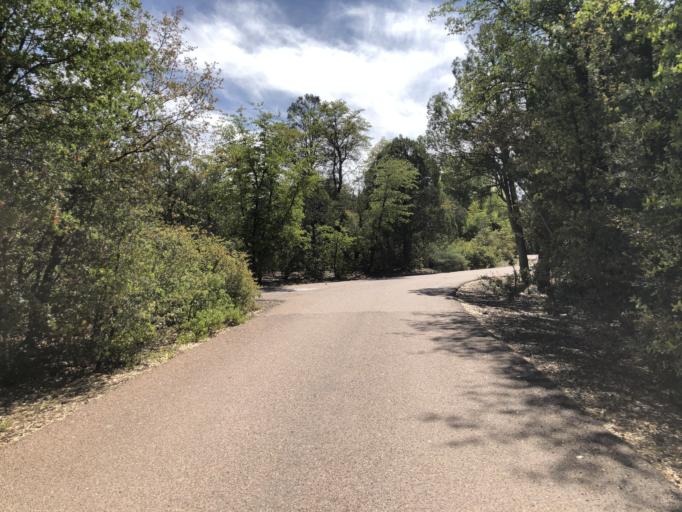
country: US
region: Arizona
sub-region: Gila County
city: Payson
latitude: 34.2722
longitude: -111.3154
